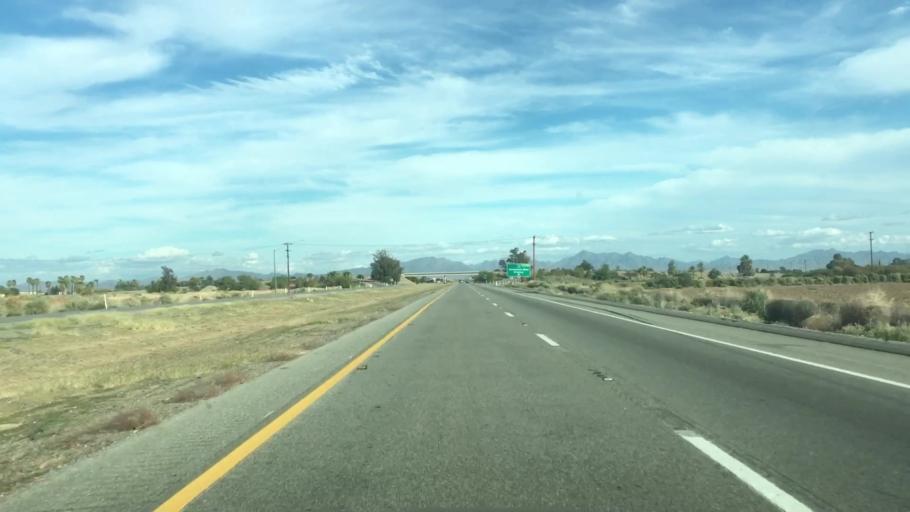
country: US
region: California
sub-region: Riverside County
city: Mesa Verde
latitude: 33.6065
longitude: -114.6644
